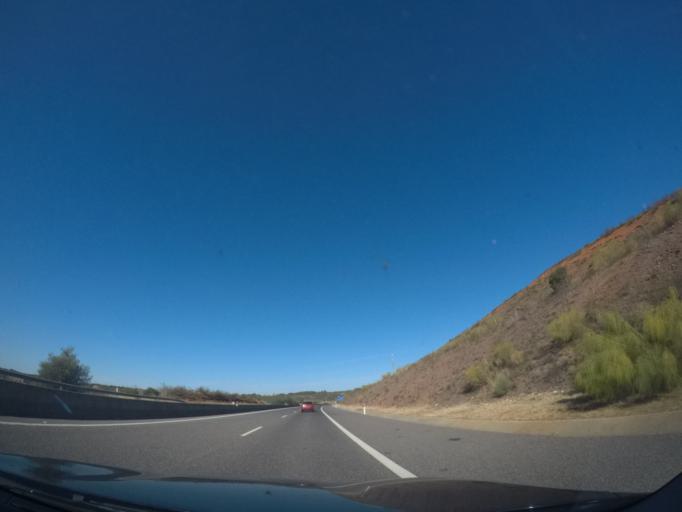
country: PT
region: Faro
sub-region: Lagos
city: Lagos
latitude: 37.1660
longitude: -8.6717
